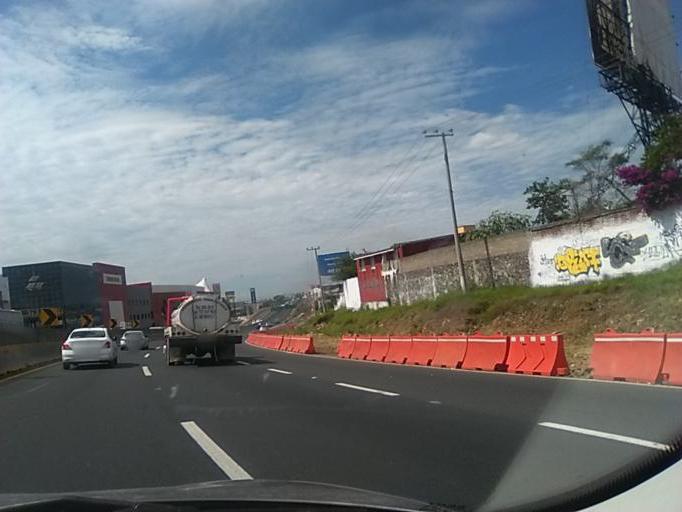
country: MX
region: Morelos
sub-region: Cuernavaca
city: Colonia los Cerritos
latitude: 18.9389
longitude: -99.1903
